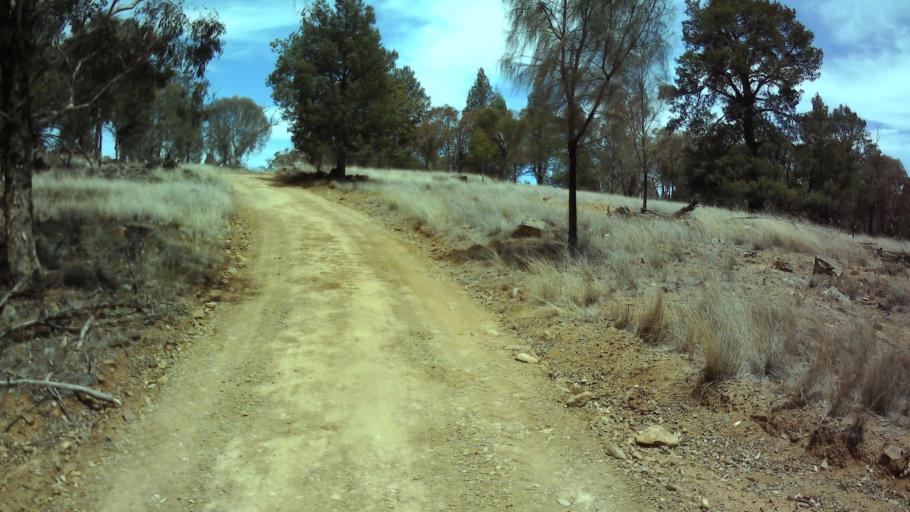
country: AU
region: New South Wales
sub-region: Weddin
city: Grenfell
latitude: -33.7870
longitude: 148.1556
